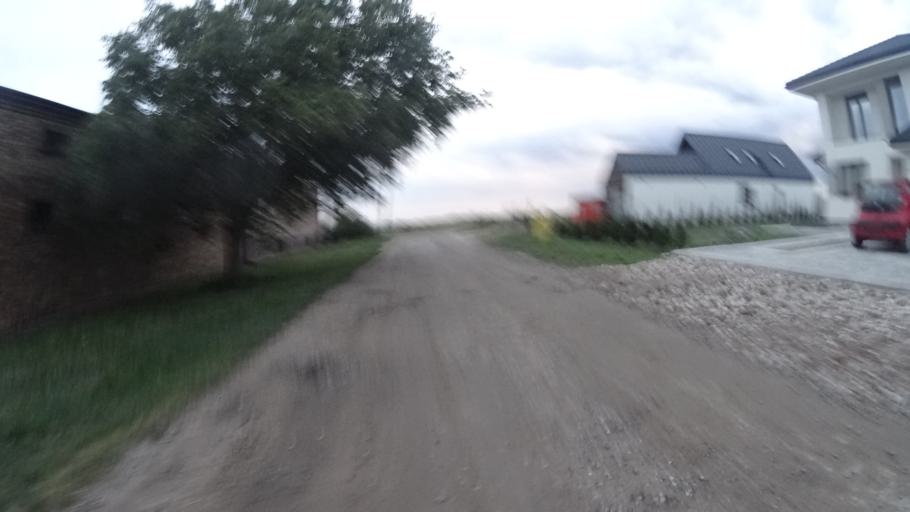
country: PL
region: Masovian Voivodeship
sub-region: Powiat warszawski zachodni
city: Ozarow Mazowiecki
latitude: 52.2296
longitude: 20.7905
